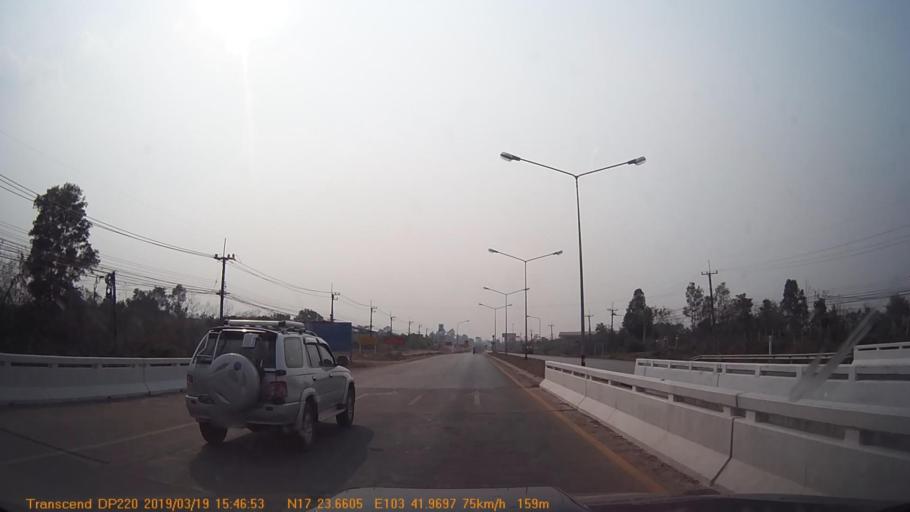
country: TH
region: Sakon Nakhon
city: Phang Khon
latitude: 17.3944
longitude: 103.6993
